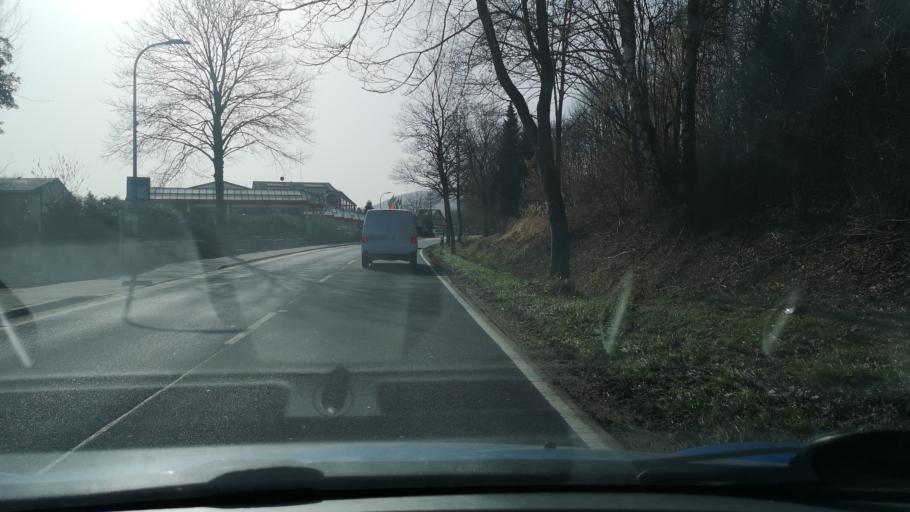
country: DE
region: Lower Saxony
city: Salzhemmendorf
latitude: 52.0699
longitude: 9.5851
